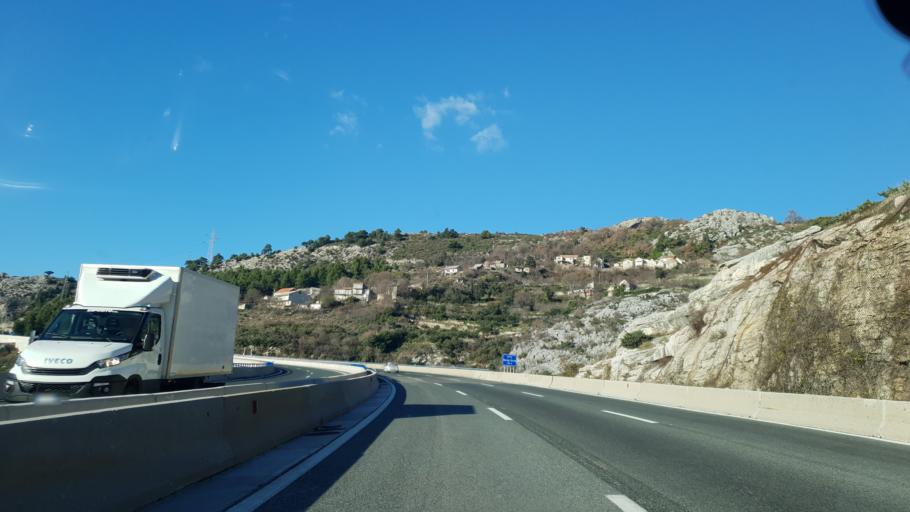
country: HR
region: Splitsko-Dalmatinska
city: Klis
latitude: 43.5583
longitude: 16.5384
